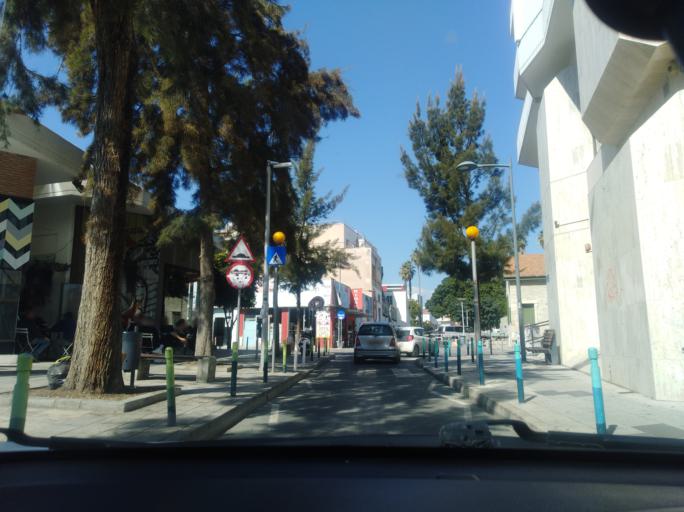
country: CY
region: Limassol
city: Limassol
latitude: 34.6758
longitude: 33.0448
